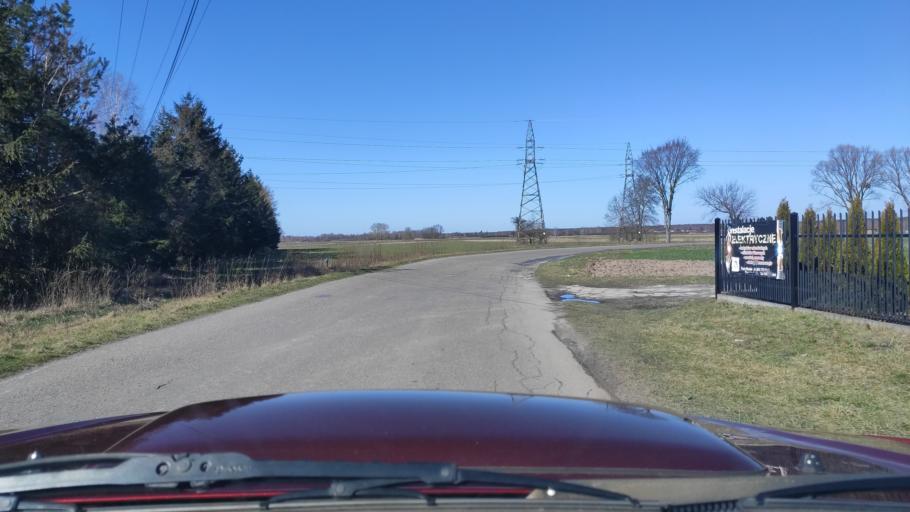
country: PL
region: Masovian Voivodeship
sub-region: Powiat zwolenski
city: Zwolen
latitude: 51.3732
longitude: 21.5829
